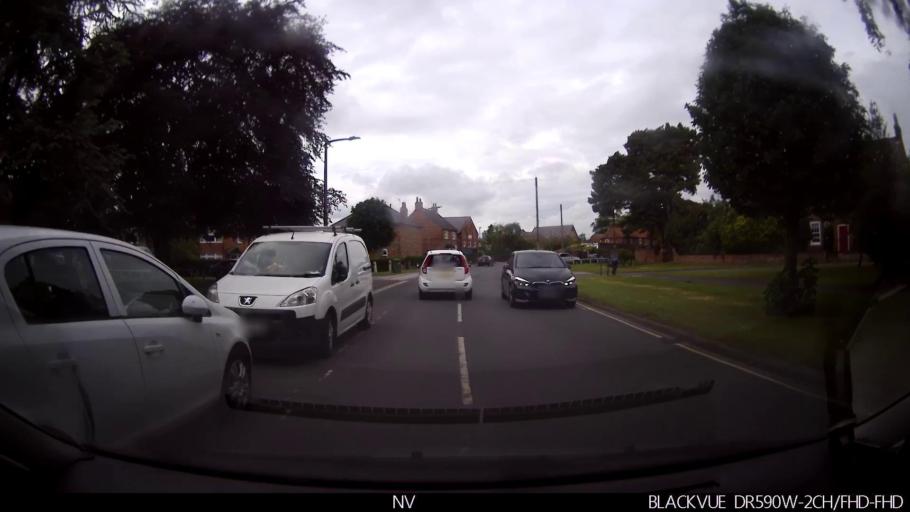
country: GB
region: England
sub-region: City of York
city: Wigginton
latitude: 54.0171
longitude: -1.0790
